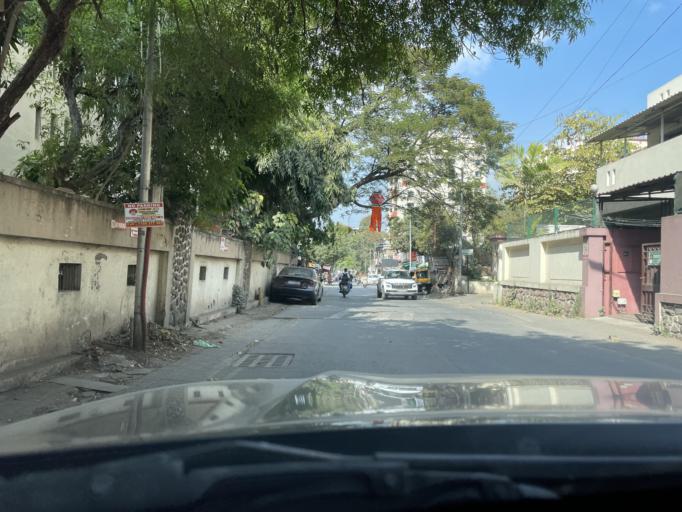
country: IN
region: Maharashtra
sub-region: Pune Division
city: Pune
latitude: 18.4825
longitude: 73.9006
